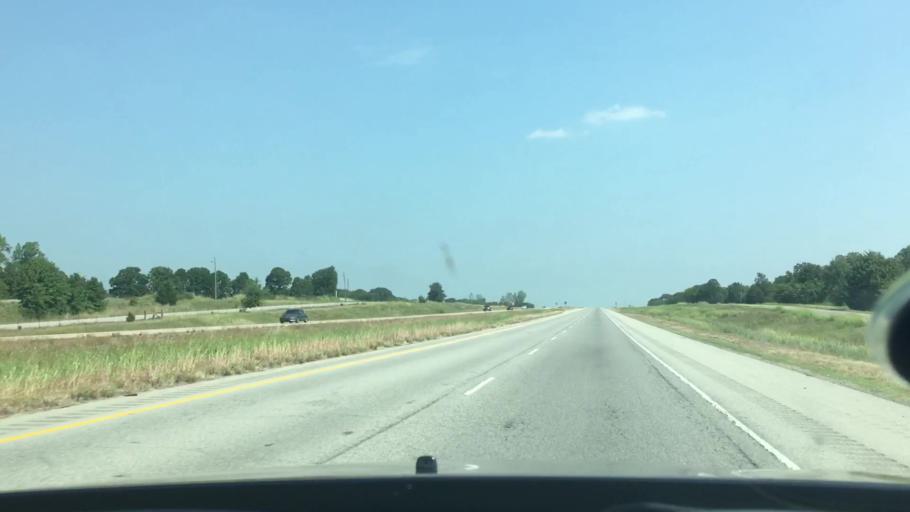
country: US
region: Oklahoma
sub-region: Atoka County
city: Atoka
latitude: 34.2772
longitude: -96.2021
